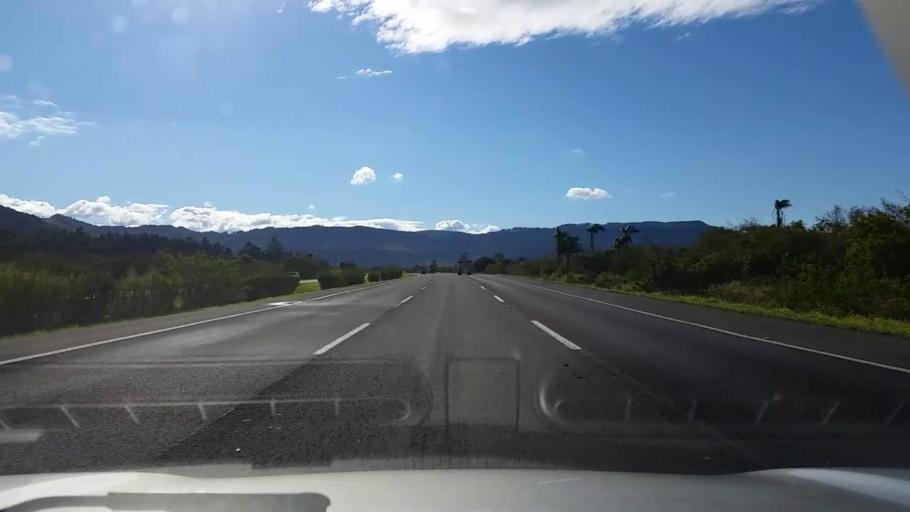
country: BR
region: Rio Grande do Sul
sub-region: Osorio
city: Osorio
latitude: -29.8821
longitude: -50.4371
